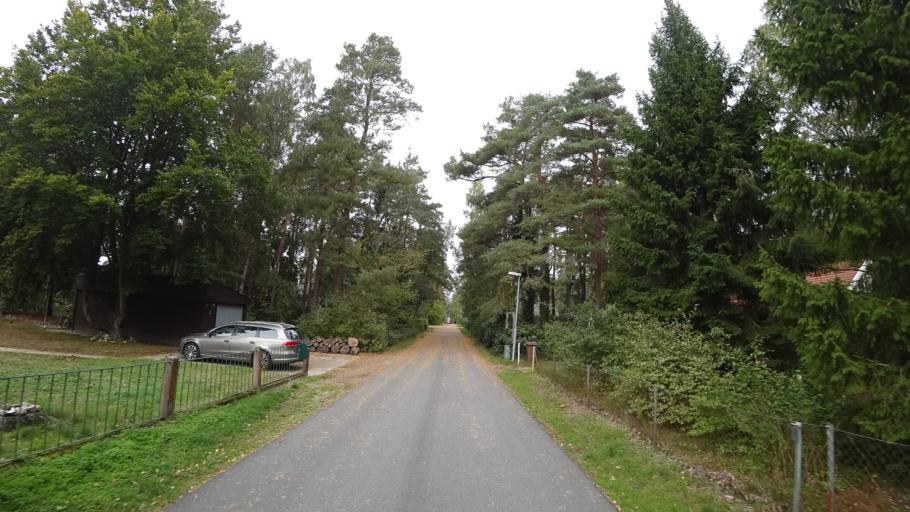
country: SE
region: Skane
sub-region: Kavlinge Kommun
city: Hofterup
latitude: 55.8009
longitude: 12.9895
